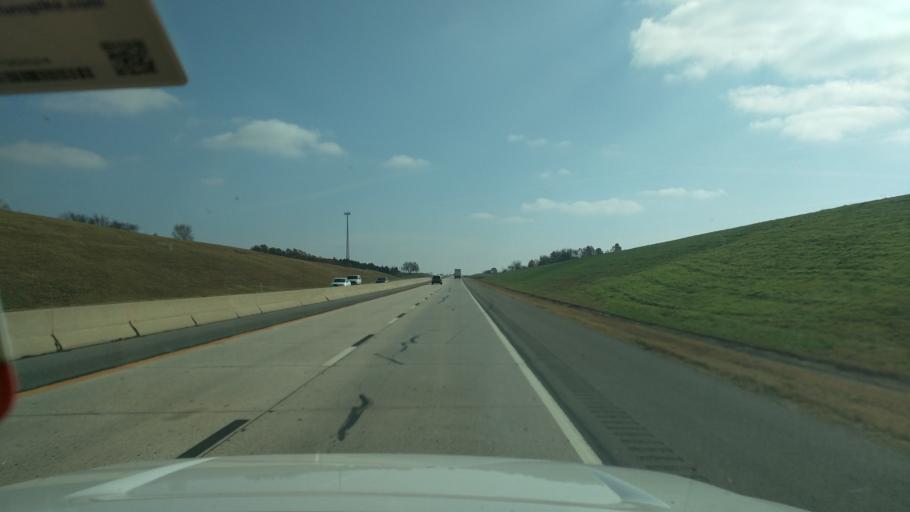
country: US
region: Oklahoma
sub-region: Wagoner County
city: Wagoner
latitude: 35.8894
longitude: -95.5001
